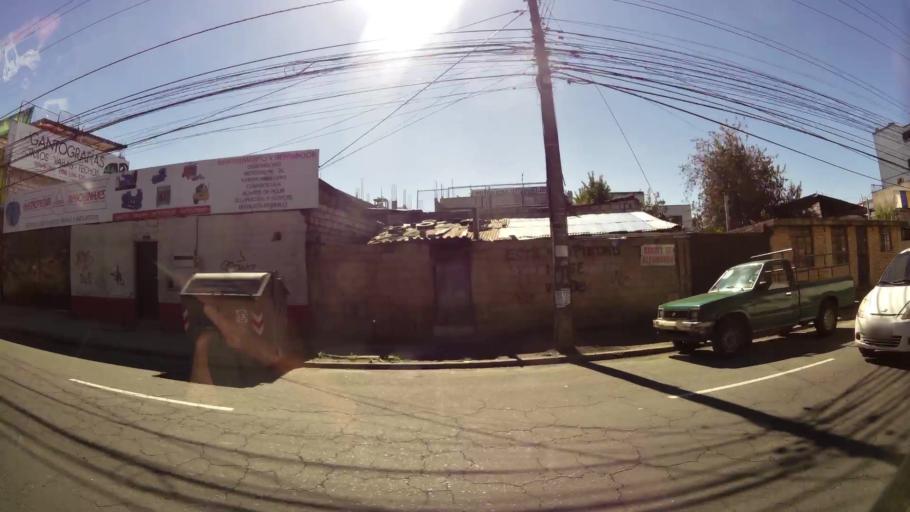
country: EC
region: Pichincha
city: Quito
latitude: -0.1289
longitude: -78.4767
